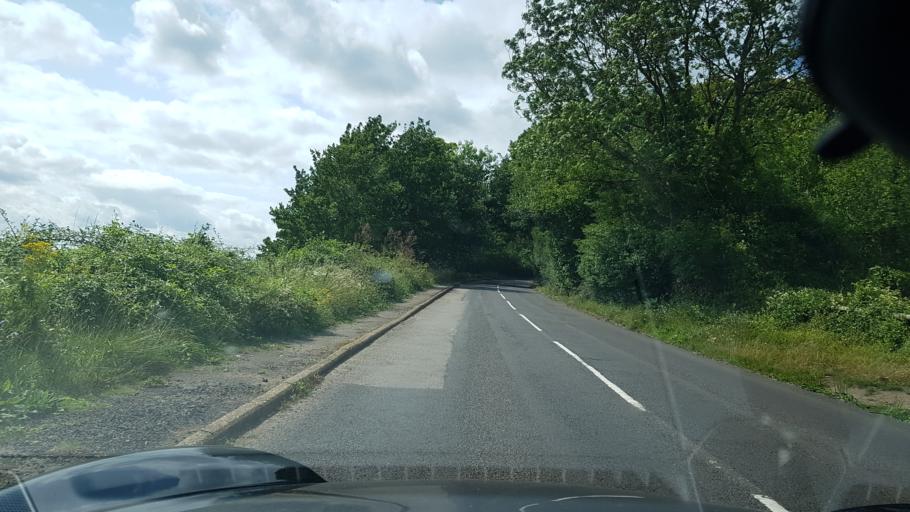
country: GB
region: England
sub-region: Surrey
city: Seale
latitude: 51.2249
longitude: -0.7217
